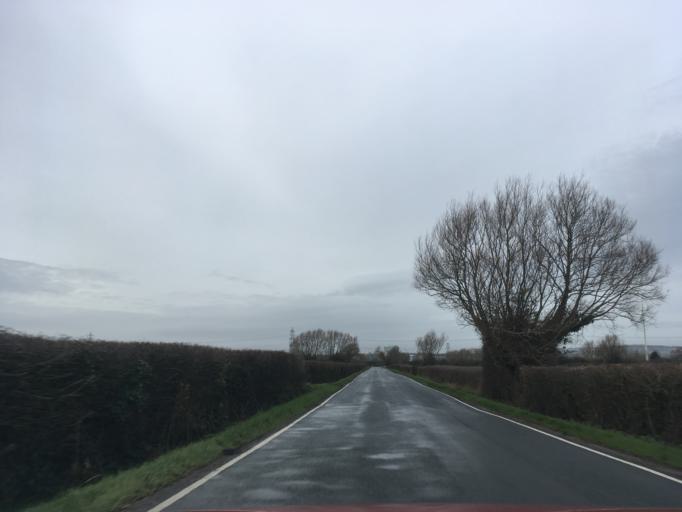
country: GB
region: Wales
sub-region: Newport
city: Redwick
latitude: 51.5615
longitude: -2.8634
